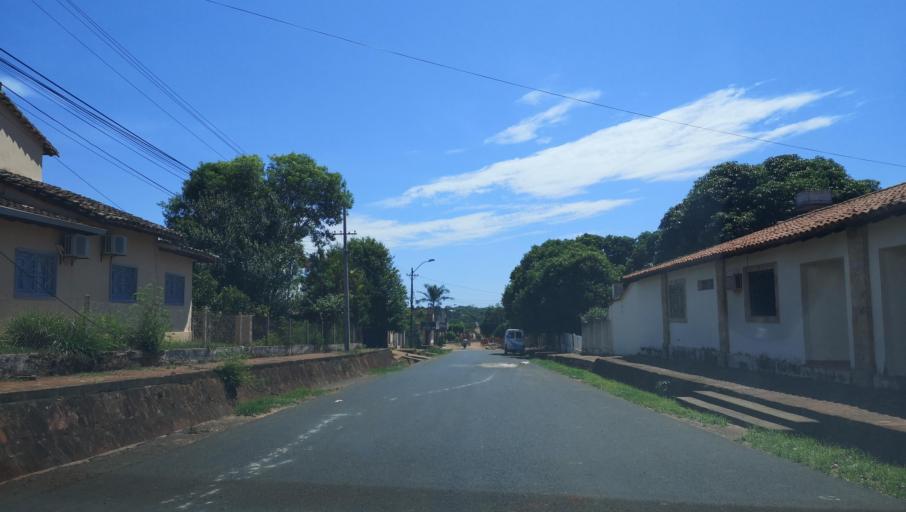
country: PY
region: Misiones
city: Santa Maria
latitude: -26.8892
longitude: -57.0292
